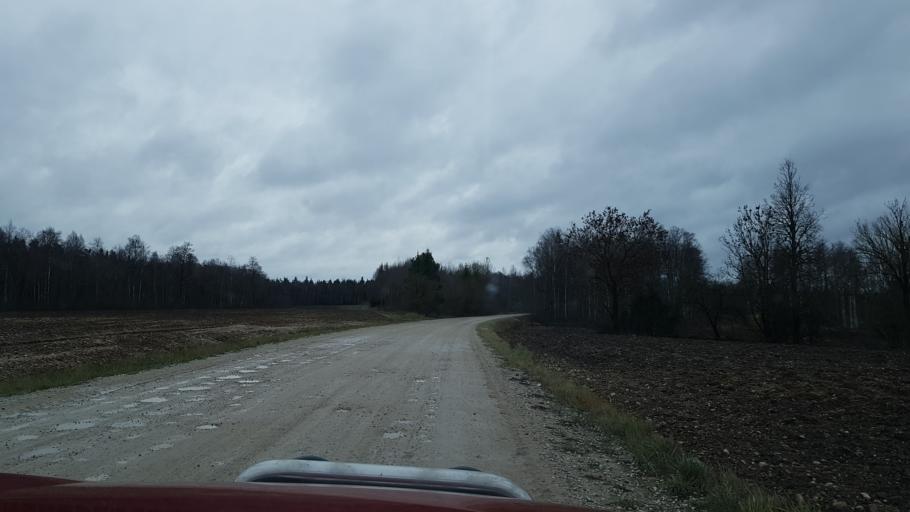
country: EE
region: Paernumaa
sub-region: Halinga vald
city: Parnu-Jaagupi
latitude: 58.5620
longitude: 24.4131
